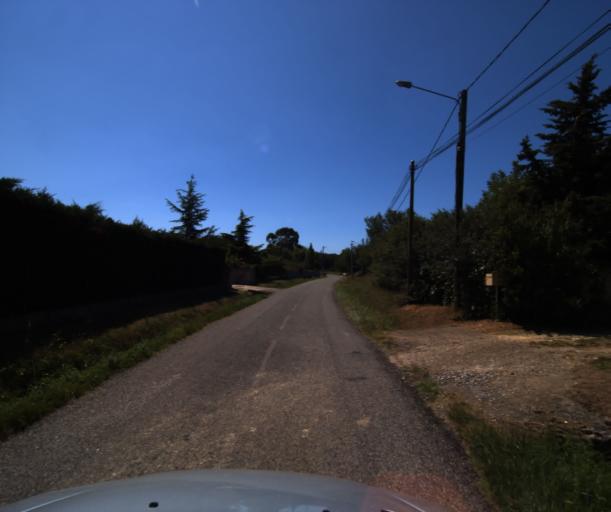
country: FR
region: Midi-Pyrenees
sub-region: Departement de la Haute-Garonne
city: Muret
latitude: 43.4549
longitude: 1.3523
